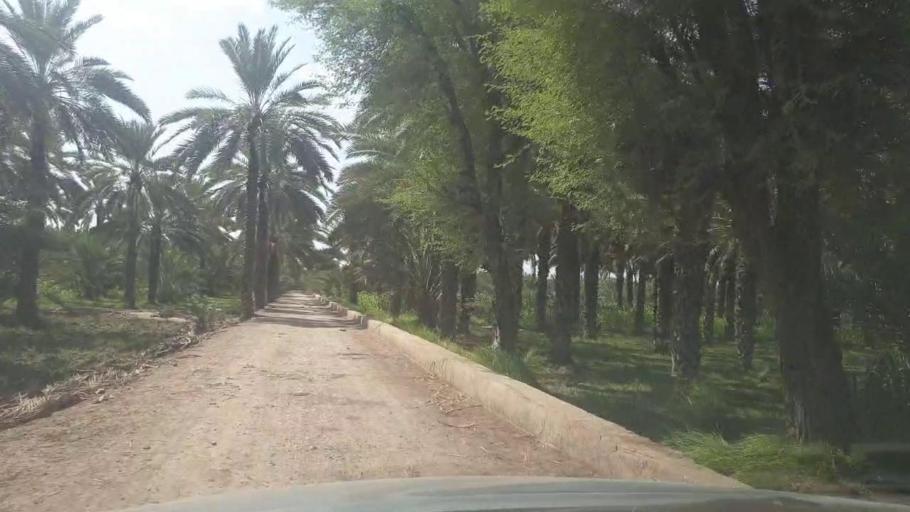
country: PK
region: Sindh
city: Khairpur
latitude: 27.5529
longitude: 68.8059
